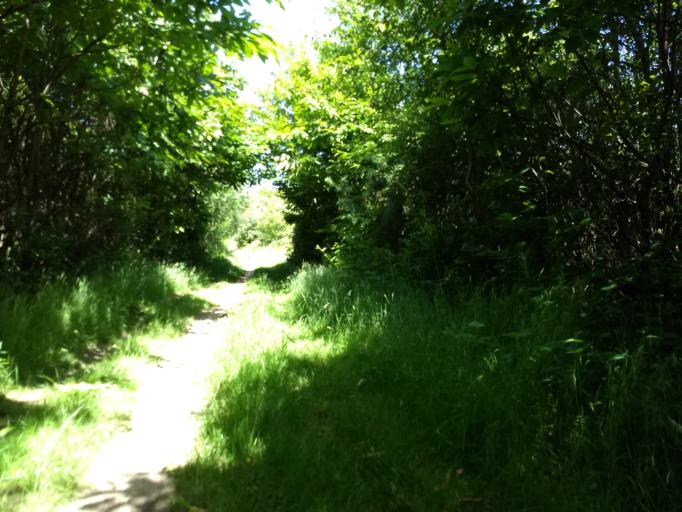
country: GB
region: England
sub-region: Isle of Wight
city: Shalfleet
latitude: 50.6565
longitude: -1.3885
